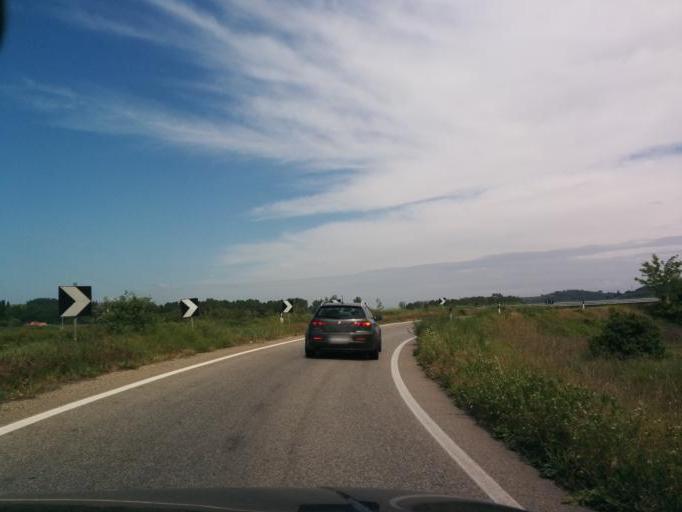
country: IT
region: Tuscany
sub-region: Provincia di Siena
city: Poggibonsi
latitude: 43.4825
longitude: 11.1251
